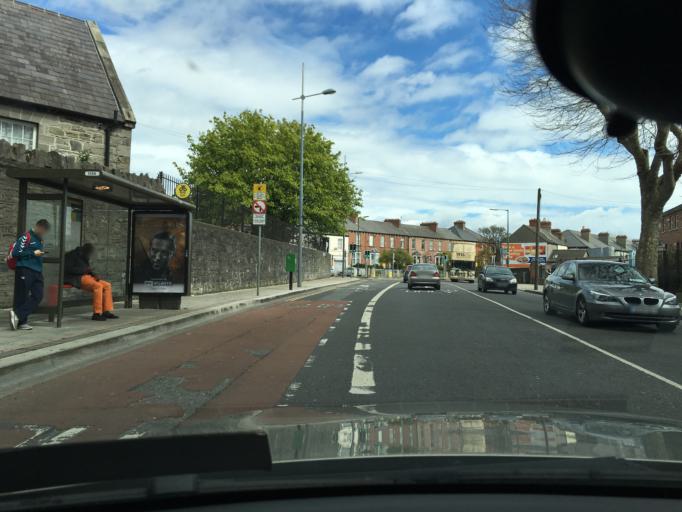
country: IE
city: Greenhills
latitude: 53.3411
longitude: -6.3199
